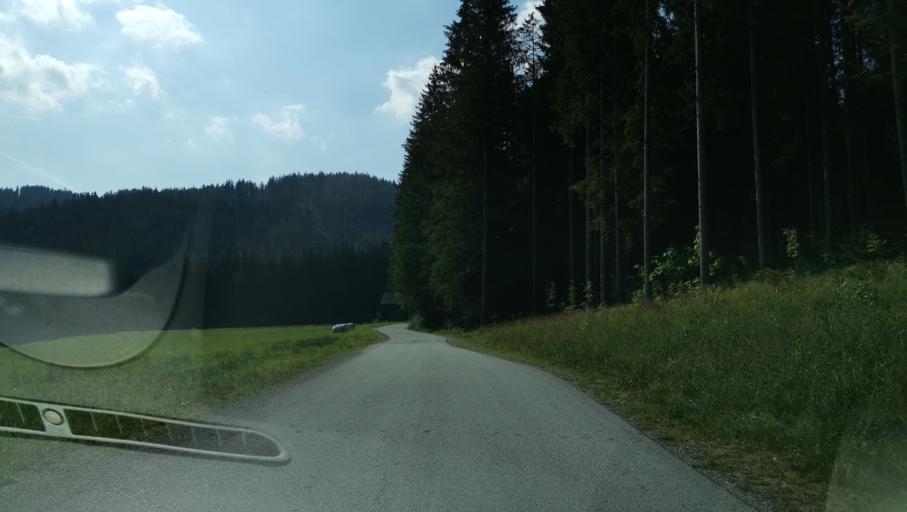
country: AT
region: Styria
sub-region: Politischer Bezirk Liezen
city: Trieben
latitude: 47.5273
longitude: 14.4683
